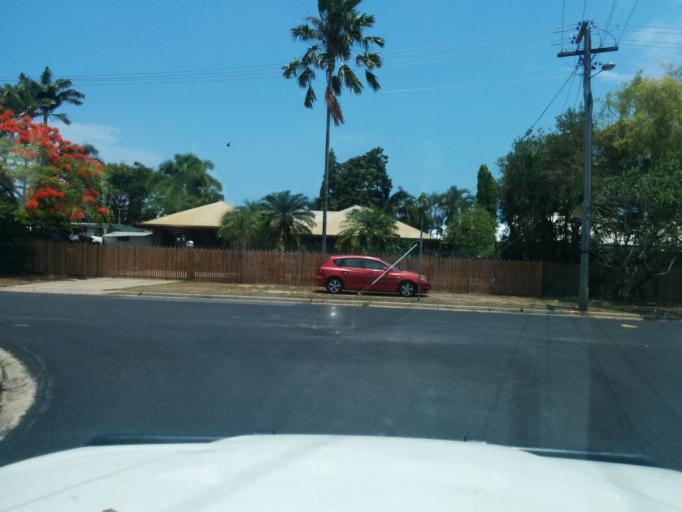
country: AU
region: Queensland
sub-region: Cairns
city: Yorkeys Knob
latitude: -16.8462
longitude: 145.7365
